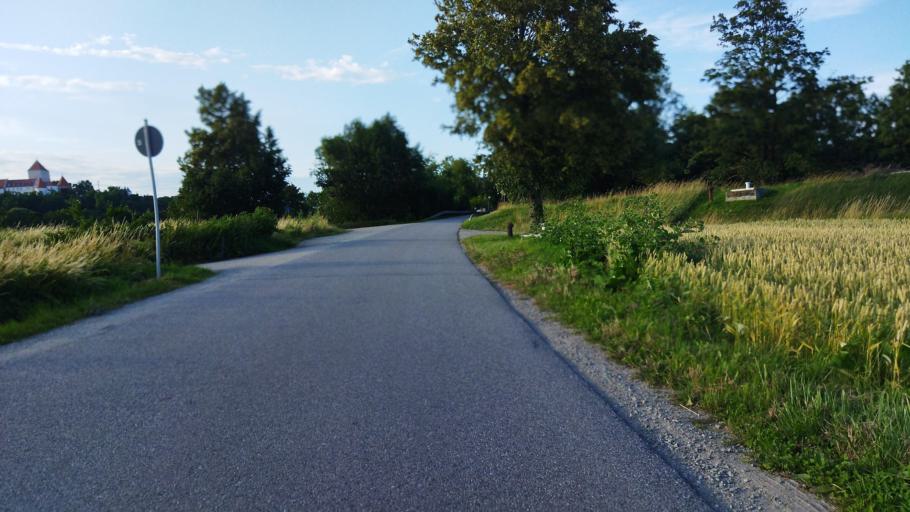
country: DE
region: Bavaria
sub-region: Upper Palatinate
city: Worth an der Donau
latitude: 48.9936
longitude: 12.4051
